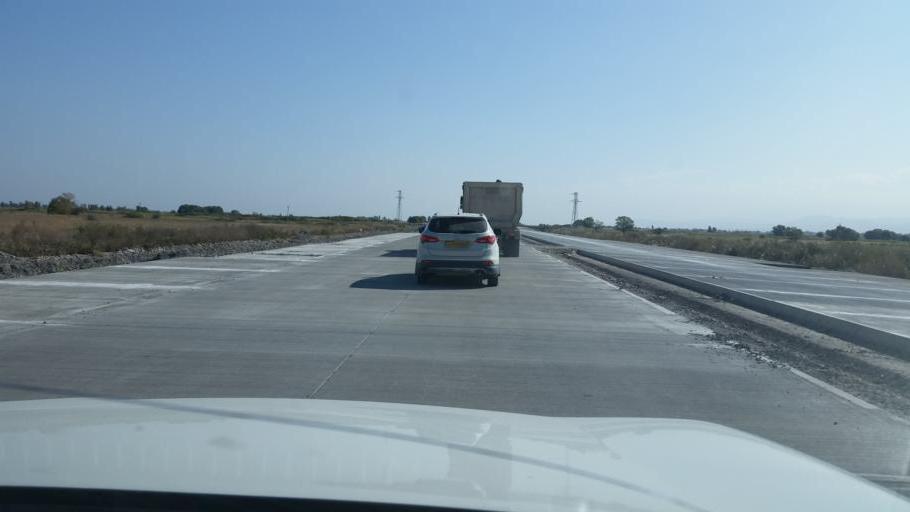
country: KZ
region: Almaty Oblysy
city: Turgen'
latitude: 43.5309
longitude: 77.5960
